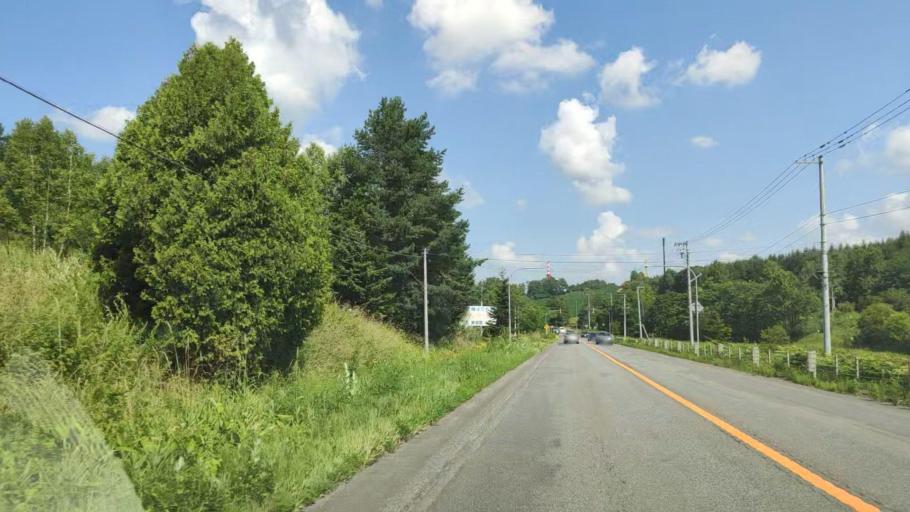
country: JP
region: Hokkaido
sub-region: Asahikawa-shi
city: Asahikawa
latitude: 43.5749
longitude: 142.4395
